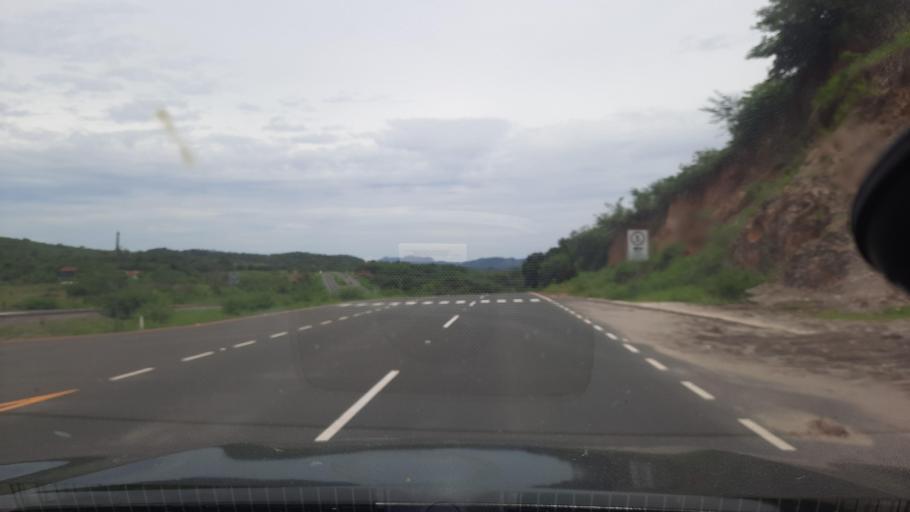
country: HN
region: Valle
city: Aramecina
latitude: 13.7472
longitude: -87.7169
